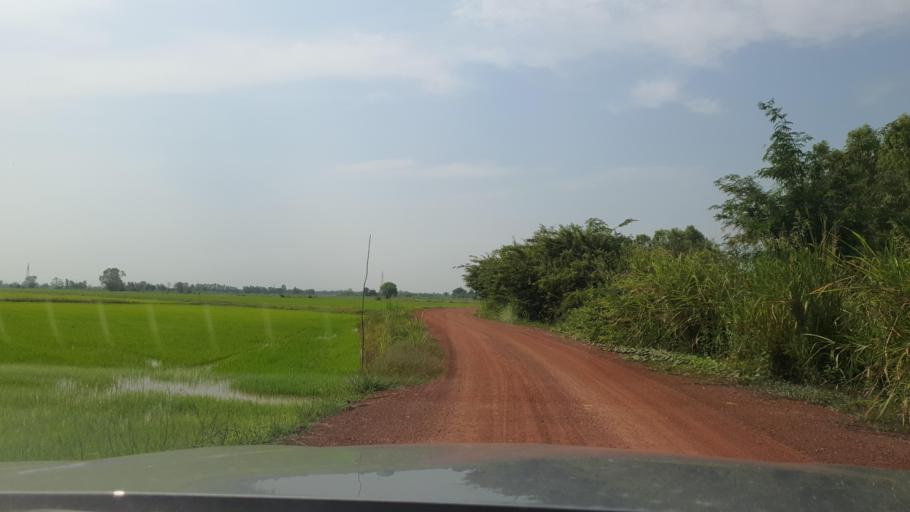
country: TH
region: Phitsanulok
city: Bang Rakam
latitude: 16.7928
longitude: 100.1086
